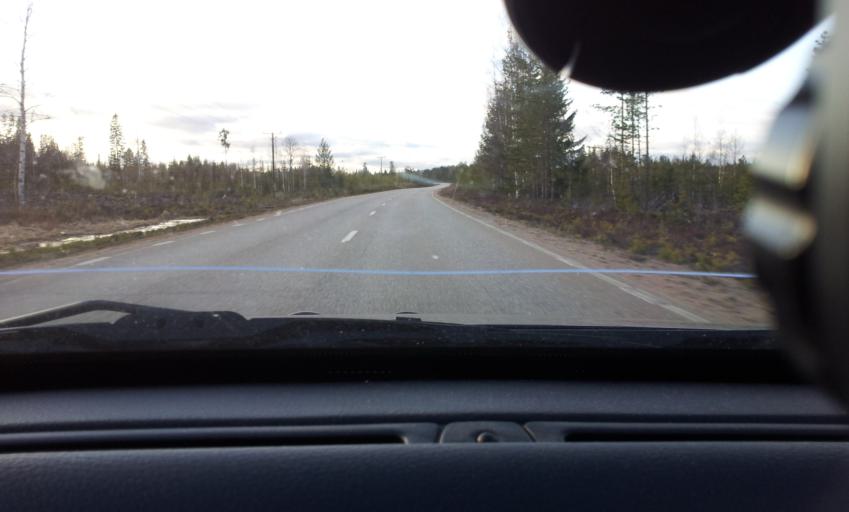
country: SE
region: Jaemtland
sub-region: Harjedalens Kommun
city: Sveg
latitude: 62.1027
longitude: 15.0697
